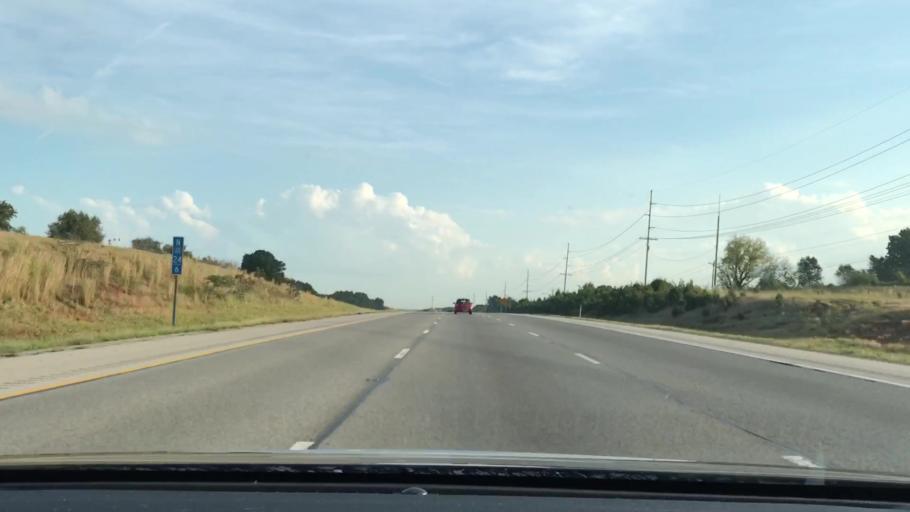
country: US
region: Kentucky
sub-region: Warren County
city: Bowling Green
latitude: 36.9621
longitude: -86.3992
